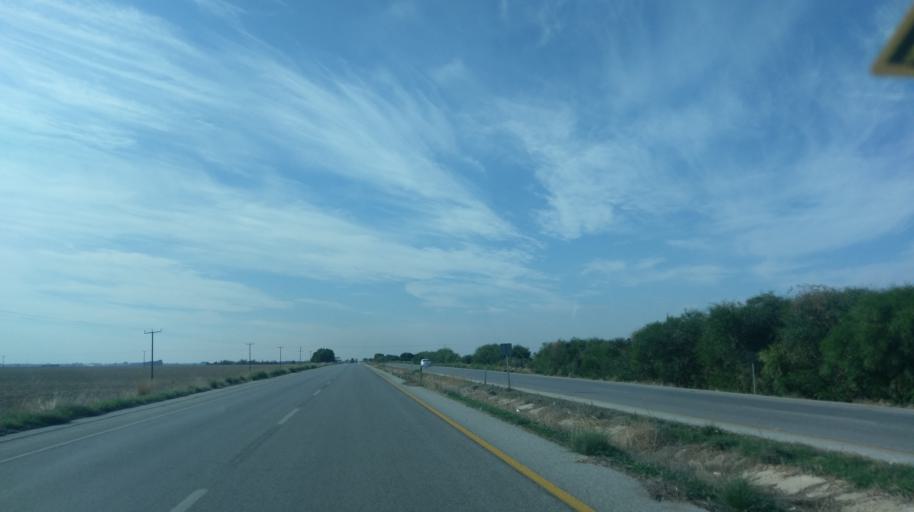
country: CY
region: Ammochostos
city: Lefkonoiko
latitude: 35.1829
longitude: 33.6949
